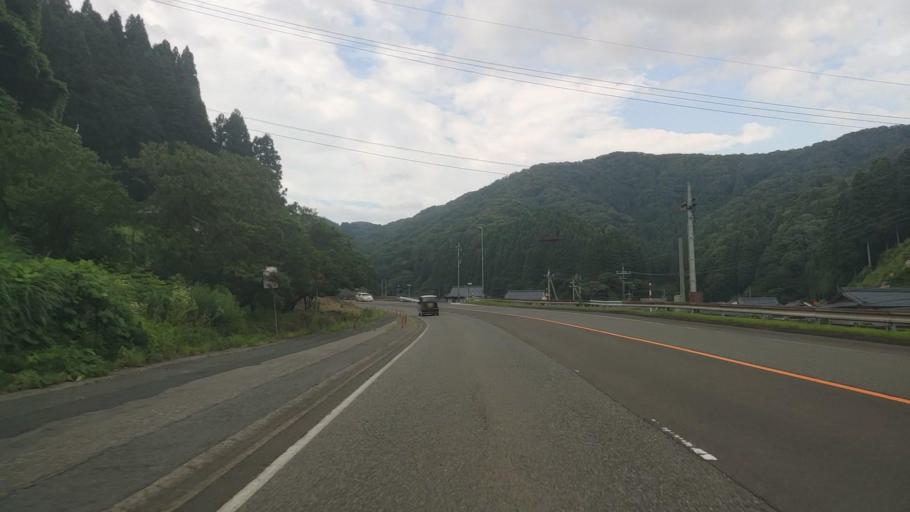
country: JP
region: Fukui
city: Takefu
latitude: 35.8326
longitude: 136.1187
